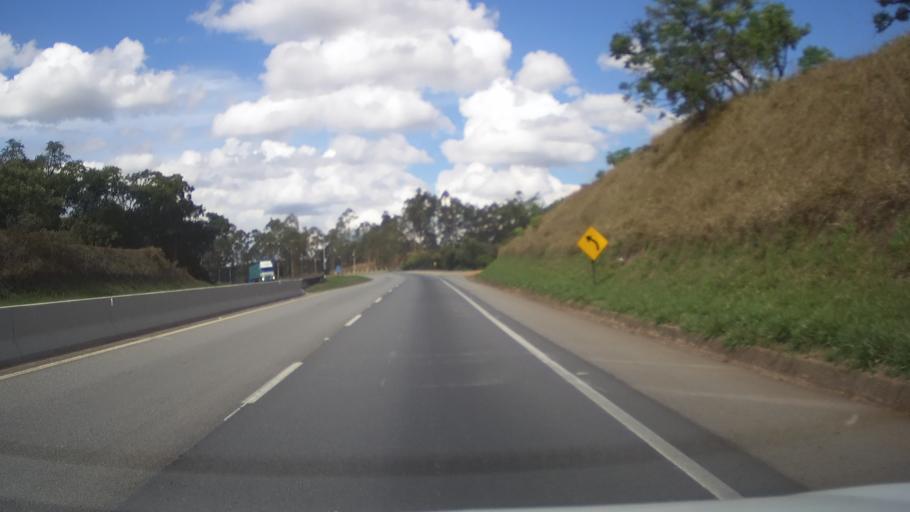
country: BR
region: Minas Gerais
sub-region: Santo Antonio Do Amparo
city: Santo Antonio do Amparo
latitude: -20.8606
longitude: -44.8385
